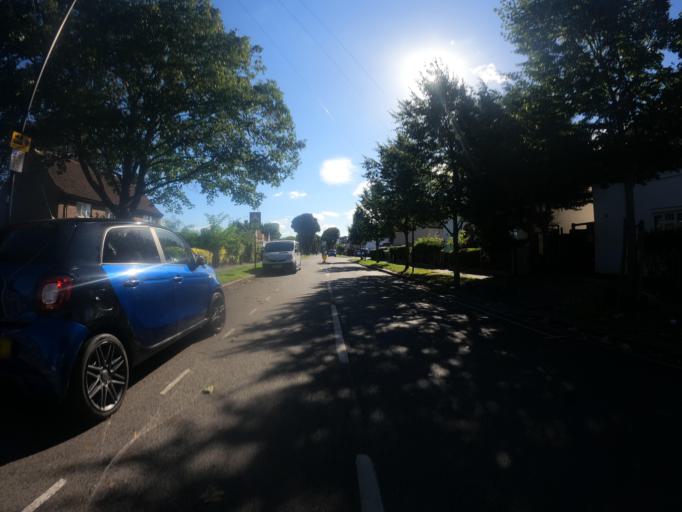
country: GB
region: England
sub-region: Greater London
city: Brentford
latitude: 51.4942
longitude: -0.3012
